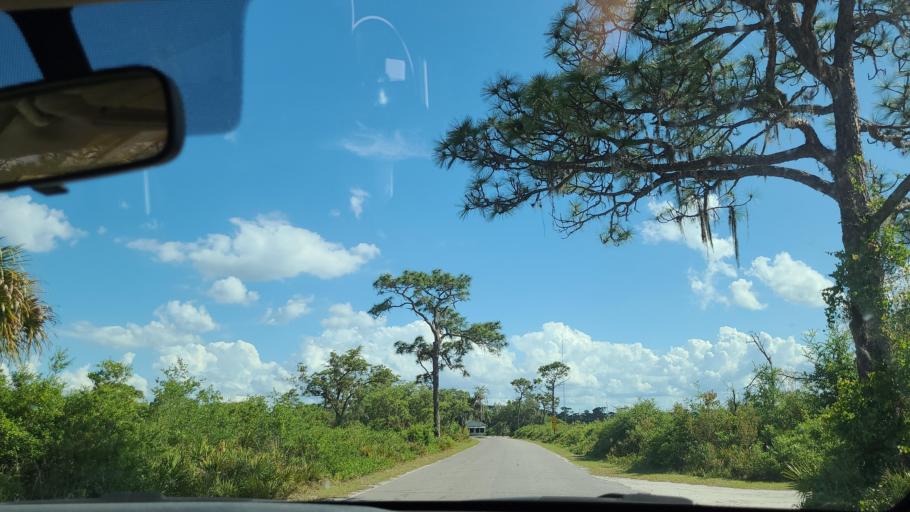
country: US
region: Florida
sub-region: Osceola County
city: Poinciana
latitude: 27.9710
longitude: -81.3803
